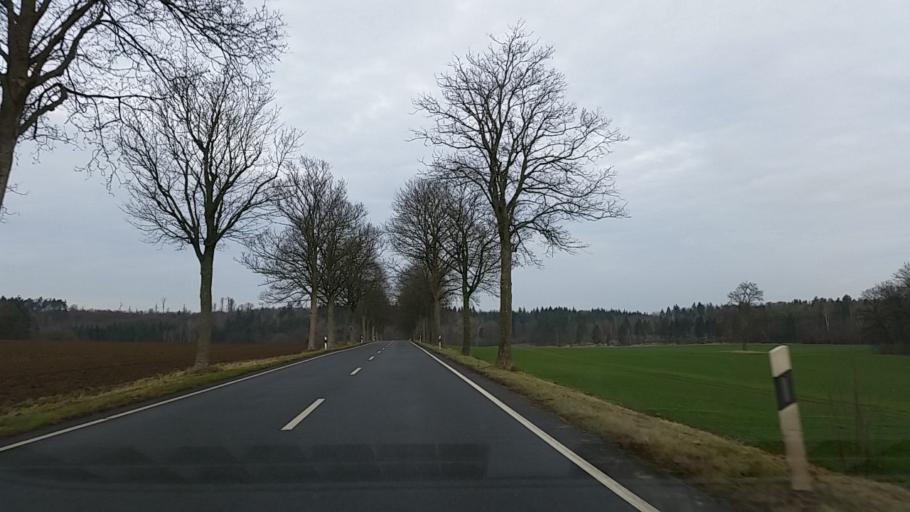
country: DE
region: Lower Saxony
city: Alt Wallmoden
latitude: 52.0057
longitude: 10.3039
